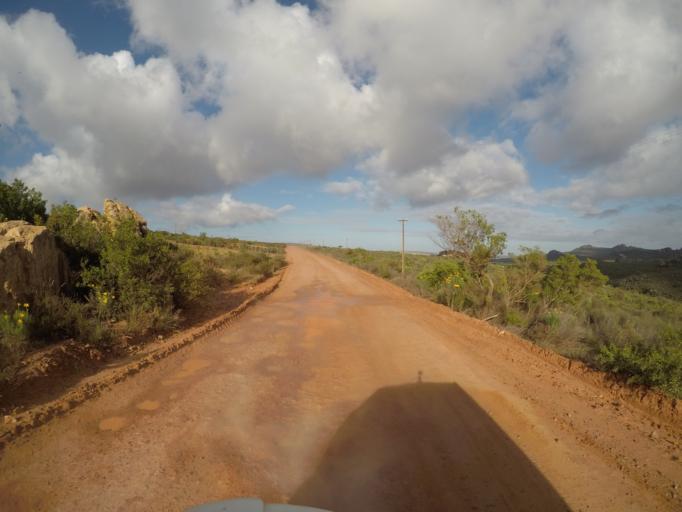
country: ZA
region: Western Cape
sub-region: West Coast District Municipality
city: Clanwilliam
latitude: -32.3415
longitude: 18.7598
